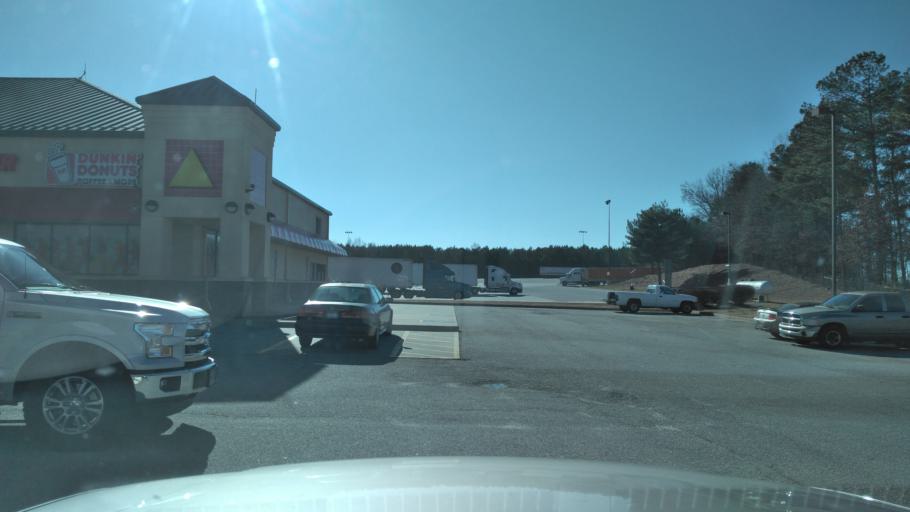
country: US
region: Georgia
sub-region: Jackson County
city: Commerce
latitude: 34.2278
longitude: -83.4993
